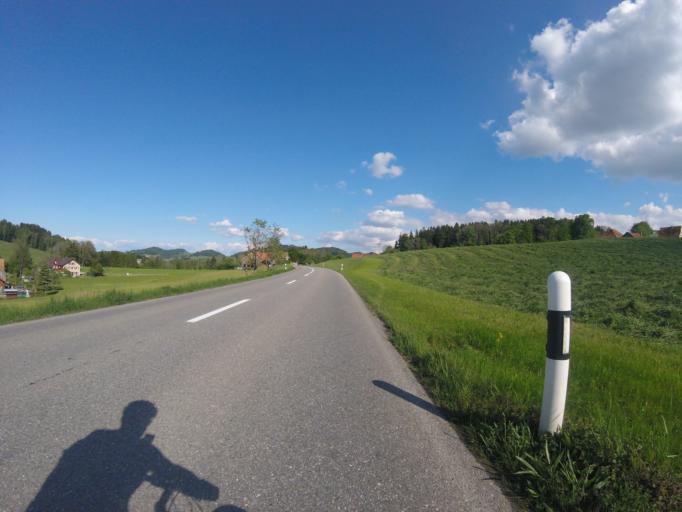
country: CH
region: Saint Gallen
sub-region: Wahlkreis Wil
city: Degersheim
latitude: 47.3854
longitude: 9.1991
